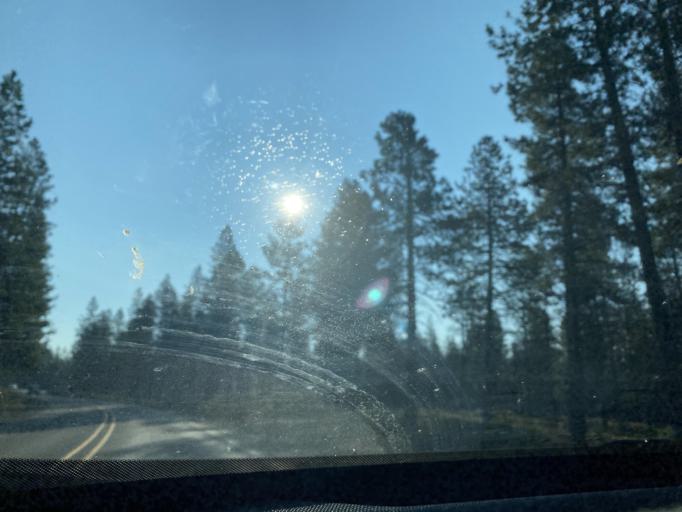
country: US
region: Oregon
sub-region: Deschutes County
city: Sunriver
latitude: 43.8694
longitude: -121.4143
